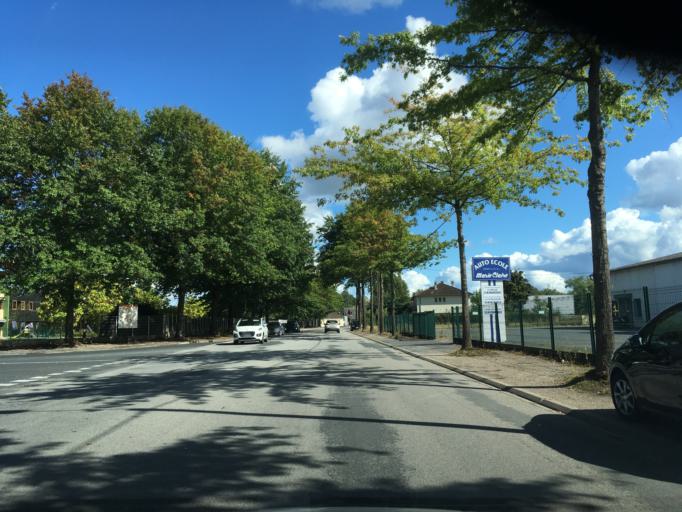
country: FR
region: Limousin
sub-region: Departement de la Correze
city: Saint-Pantaleon-de-Larche
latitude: 45.1560
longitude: 1.4778
